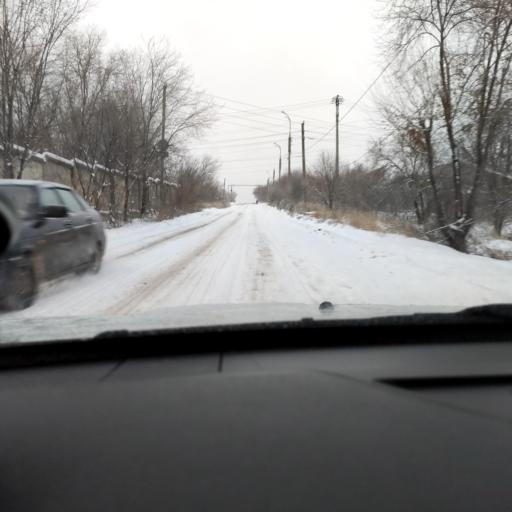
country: RU
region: Samara
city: Smyshlyayevka
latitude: 53.2380
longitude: 50.4805
